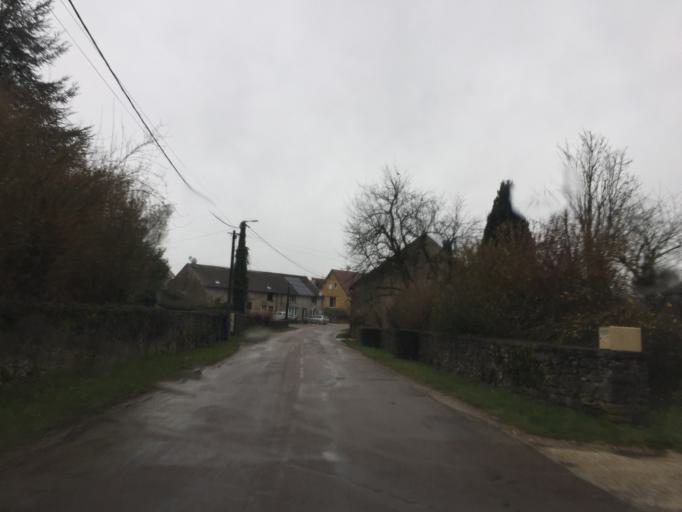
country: FR
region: Franche-Comte
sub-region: Departement du Jura
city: Dole
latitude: 47.1475
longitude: 5.5130
